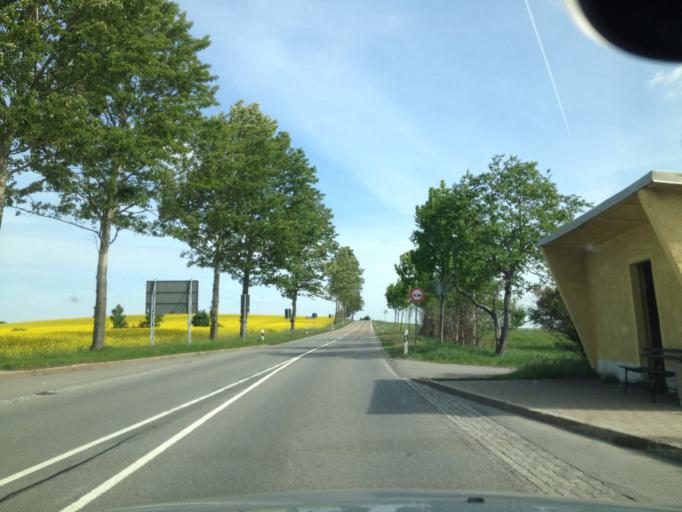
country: DE
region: Saxony
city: Annaberg-Buchholz
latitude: 50.5500
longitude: 13.0179
